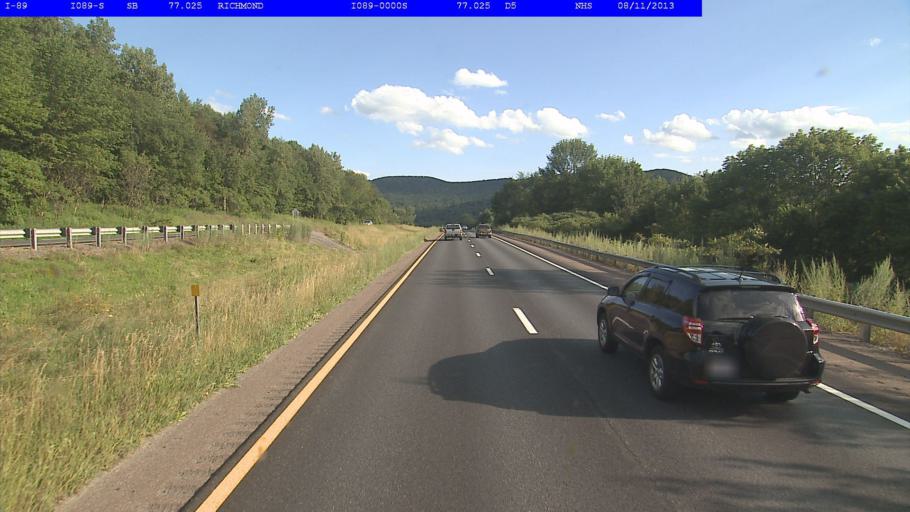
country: US
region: Vermont
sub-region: Chittenden County
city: Williston
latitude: 44.4108
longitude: -72.9911
